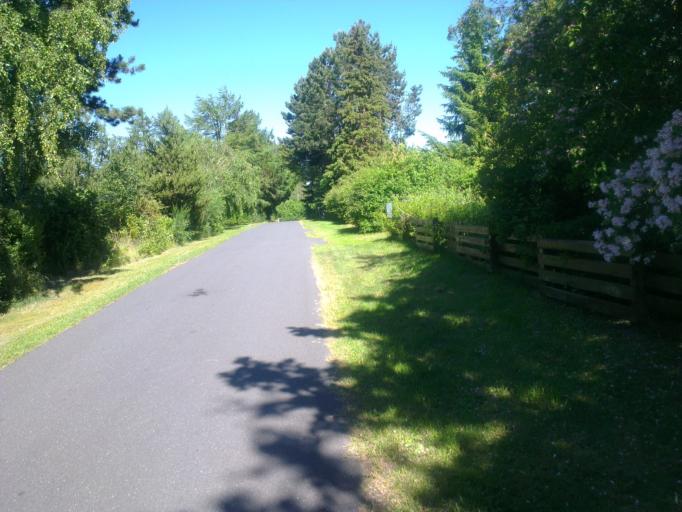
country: DK
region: Capital Region
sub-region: Halsnaes Kommune
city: Hundested
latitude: 55.9217
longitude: 11.9119
